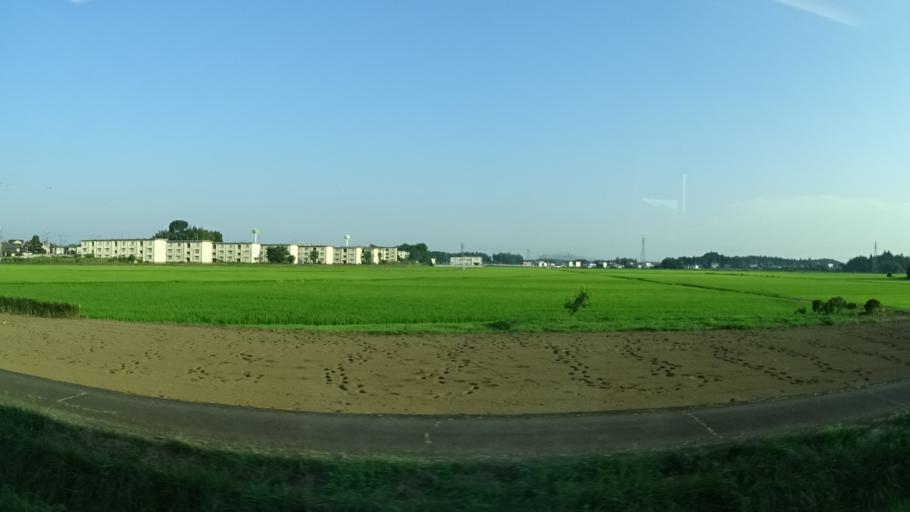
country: JP
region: Ibaraki
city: Mito-shi
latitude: 36.3793
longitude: 140.3965
